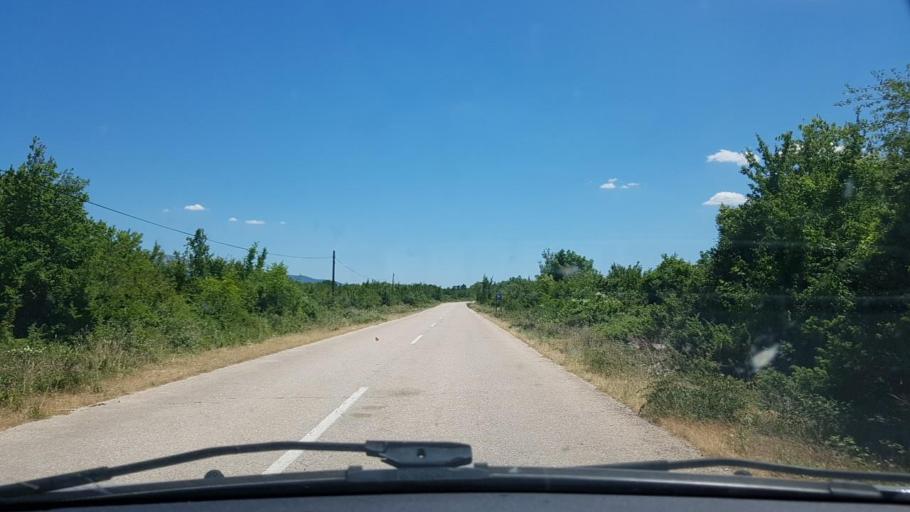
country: HR
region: Sibensko-Kniniska
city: Kistanje
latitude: 43.9690
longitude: 15.9766
